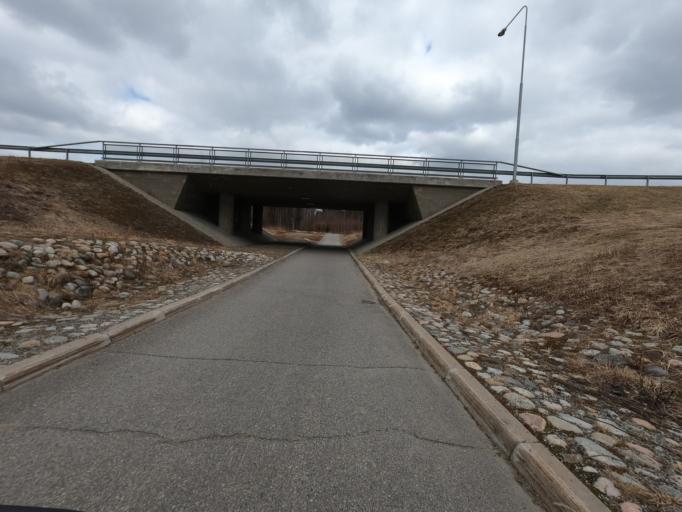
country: FI
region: North Karelia
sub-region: Joensuu
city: Joensuu
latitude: 62.5710
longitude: 29.8130
